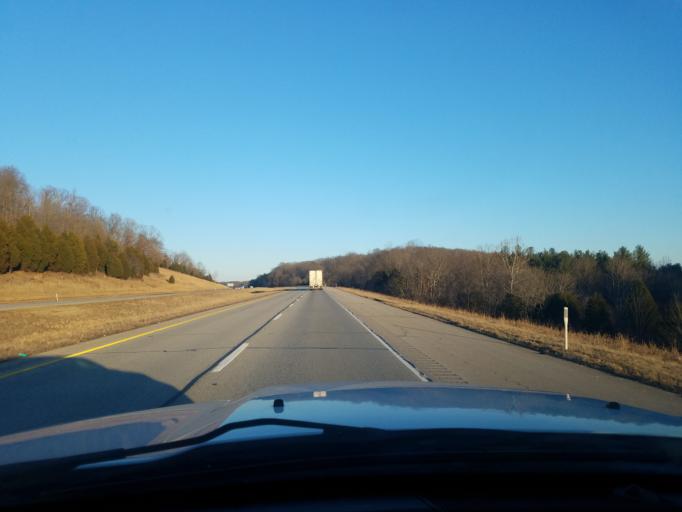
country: US
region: Indiana
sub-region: Crawford County
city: English
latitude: 38.2509
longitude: -86.3295
